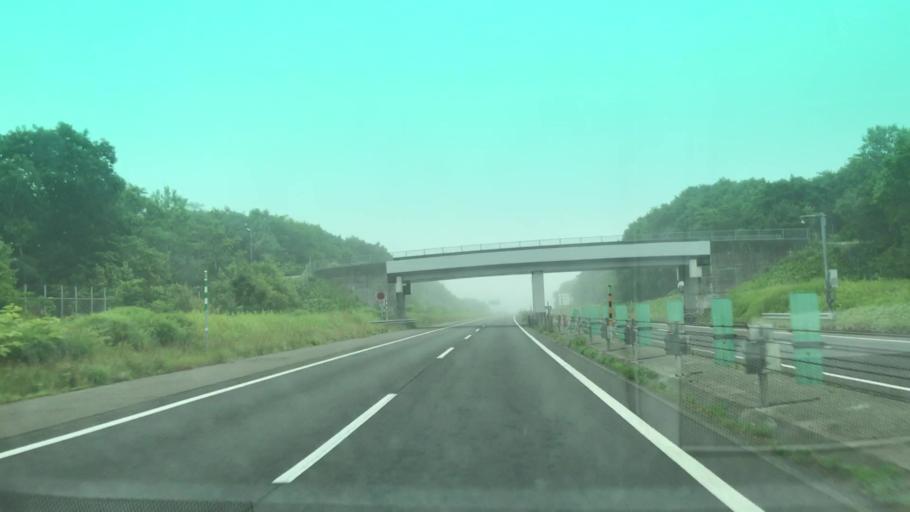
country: JP
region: Hokkaido
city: Chitose
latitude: 42.8239
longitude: 141.6159
